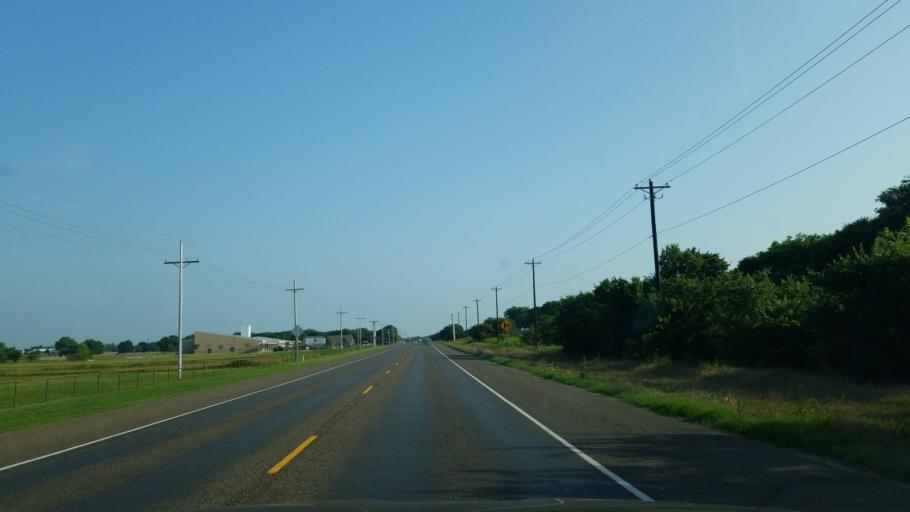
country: US
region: Texas
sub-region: Denton County
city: Aubrey
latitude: 33.3446
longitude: -96.9685
